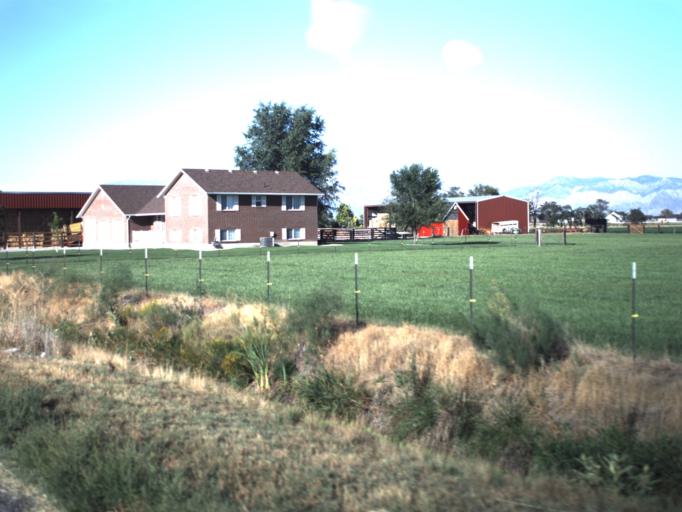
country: US
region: Utah
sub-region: Weber County
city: Hooper
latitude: 41.1550
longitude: -112.1229
